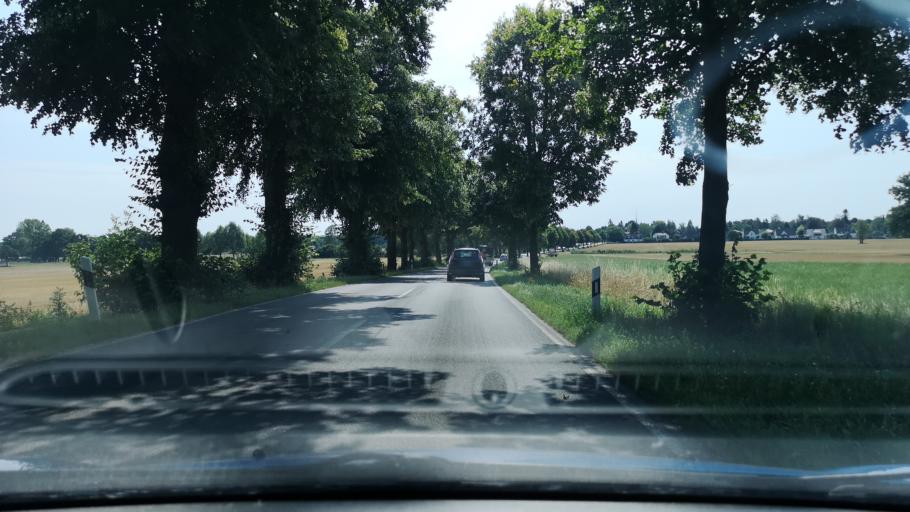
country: DE
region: Lower Saxony
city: Isernhagen Farster Bauerschaft
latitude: 52.4531
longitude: 9.7990
